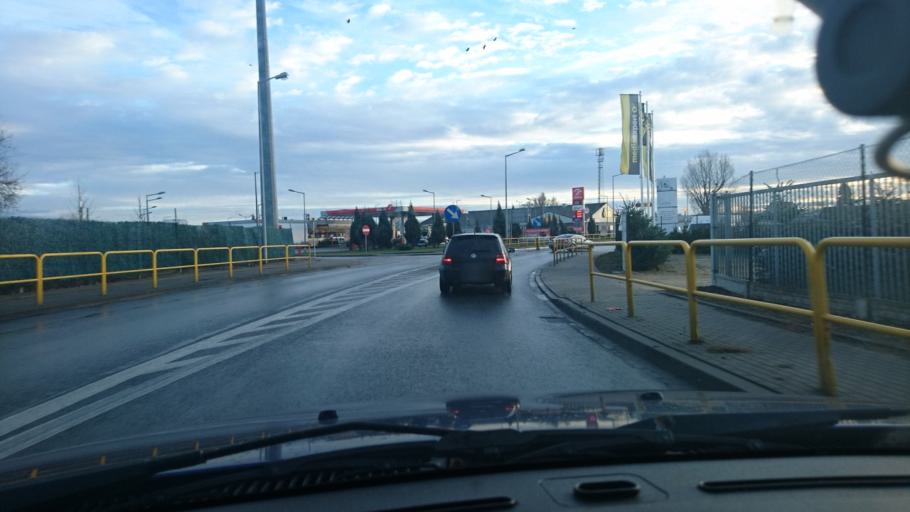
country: PL
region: Greater Poland Voivodeship
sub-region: Powiat kepinski
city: Kepno
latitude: 51.2820
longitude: 17.9923
